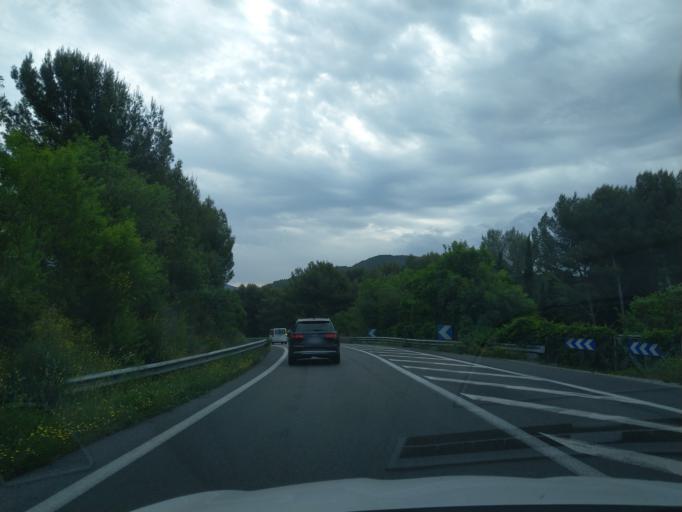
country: FR
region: Provence-Alpes-Cote d'Azur
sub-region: Departement des Bouches-du-Rhone
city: Aubagne
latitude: 43.2828
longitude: 5.5763
